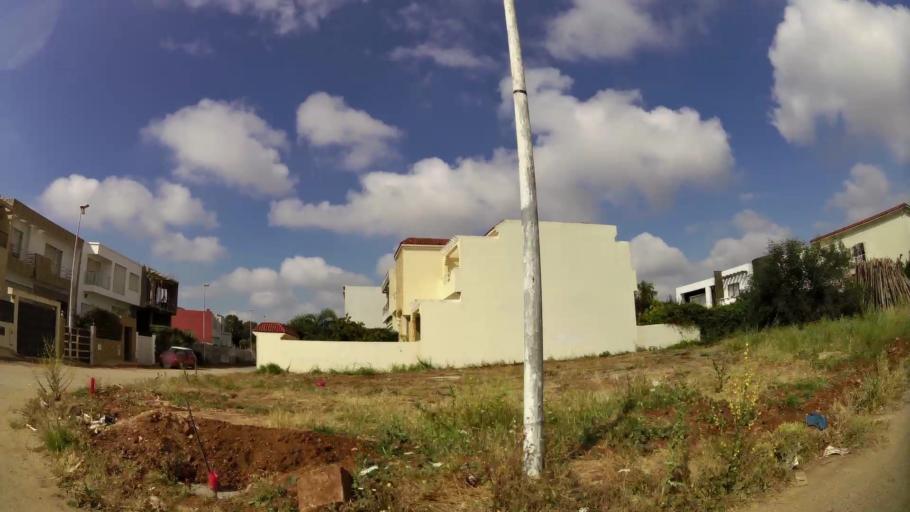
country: MA
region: Rabat-Sale-Zemmour-Zaer
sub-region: Skhirate-Temara
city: Temara
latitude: 33.9523
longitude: -6.8799
